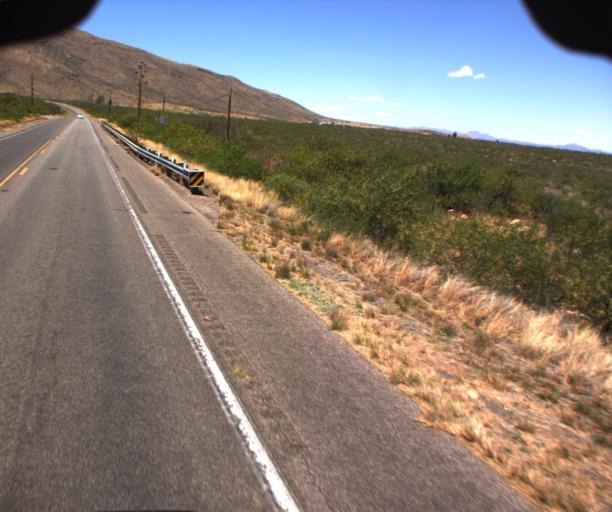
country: US
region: Arizona
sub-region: Cochise County
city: Bisbee
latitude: 31.4353
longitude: -109.8157
